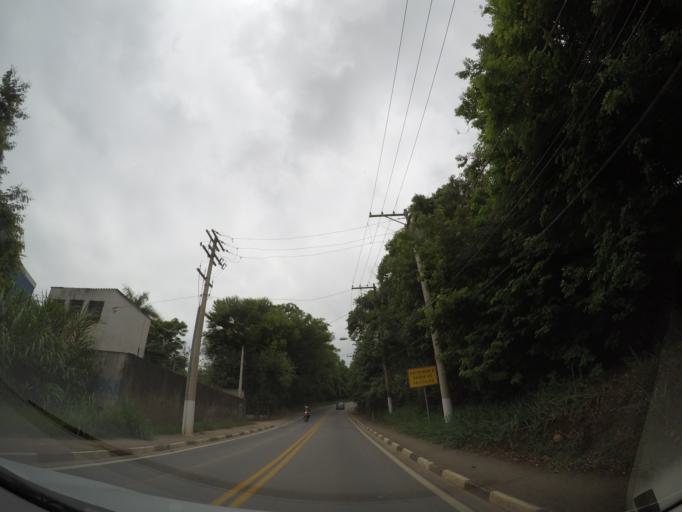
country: BR
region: Sao Paulo
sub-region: Louveira
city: Louveira
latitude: -23.0757
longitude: -46.9598
